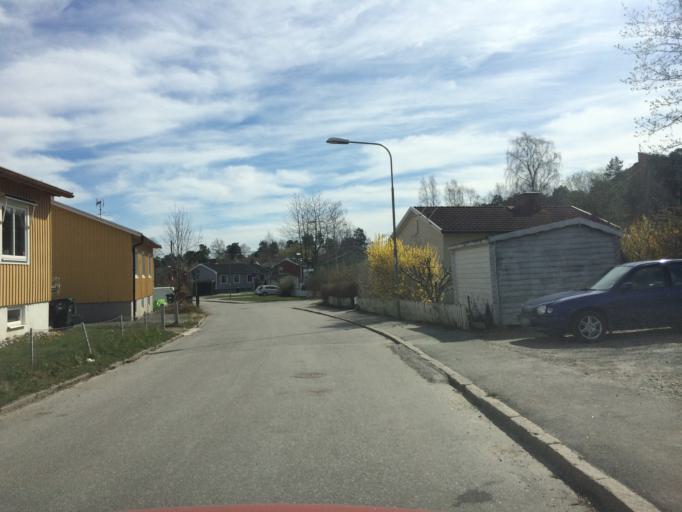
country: SE
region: Stockholm
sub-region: Huddinge Kommun
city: Huddinge
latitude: 59.2841
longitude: 17.9822
